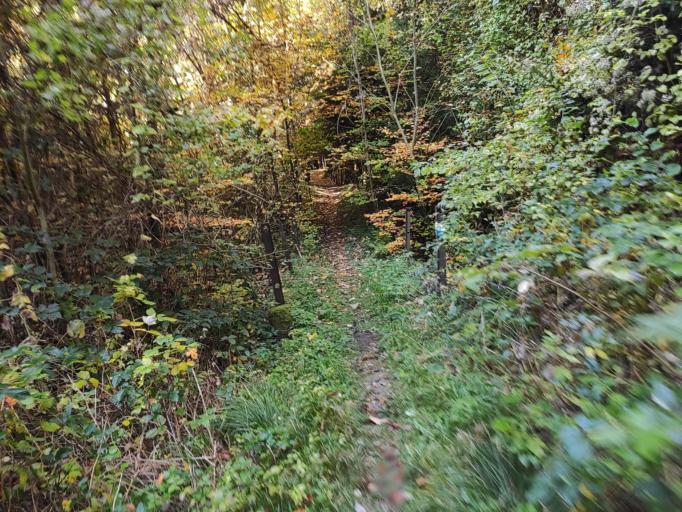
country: AT
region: Lower Austria
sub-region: Politischer Bezirk Sankt Polten
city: Pyhra
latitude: 48.1669
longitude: 15.6765
